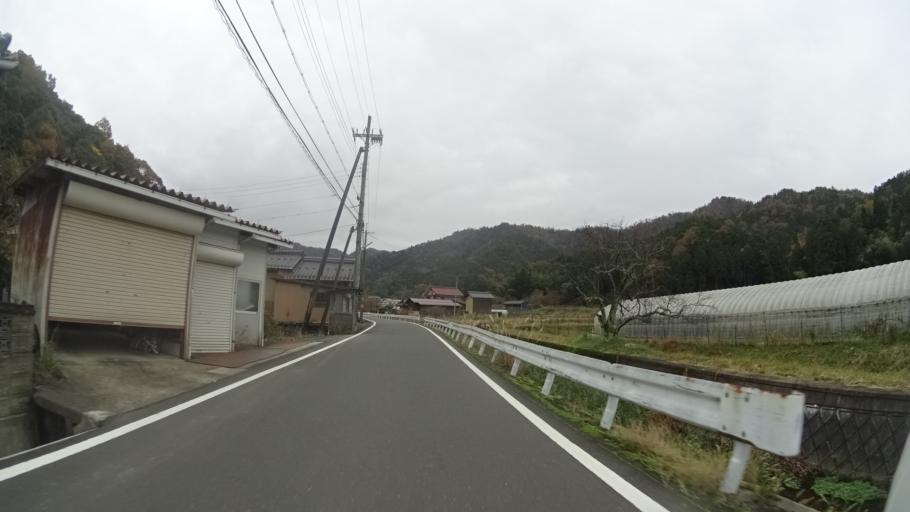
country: JP
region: Kyoto
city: Maizuru
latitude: 35.4790
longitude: 135.4425
